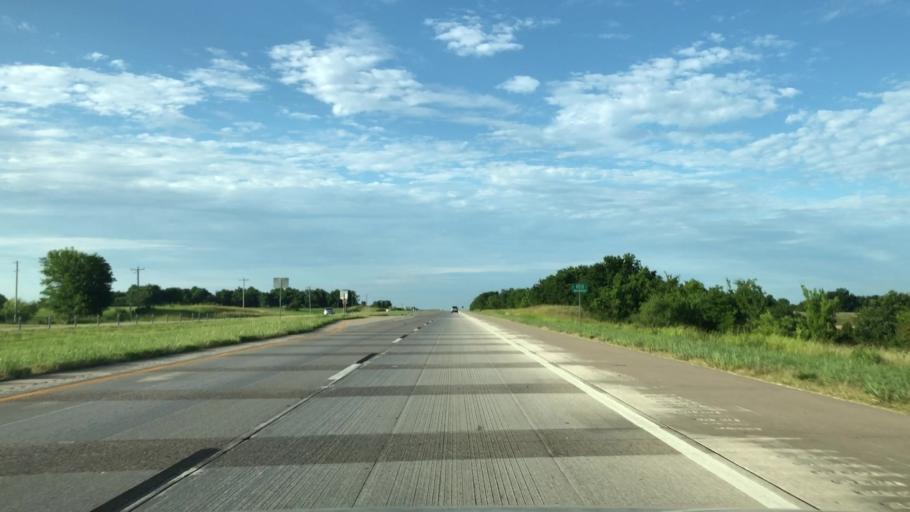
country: US
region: Oklahoma
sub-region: Osage County
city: Skiatook
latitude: 36.4320
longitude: -95.9207
